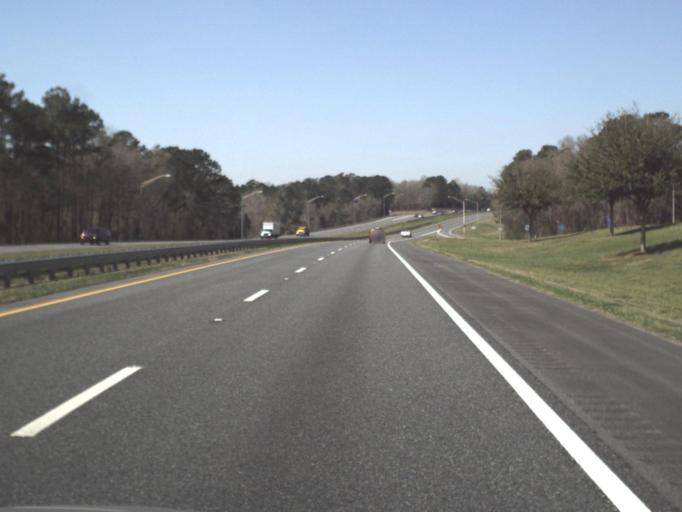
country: US
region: Florida
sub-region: Jackson County
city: Marianna
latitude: 30.7571
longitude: -85.3214
